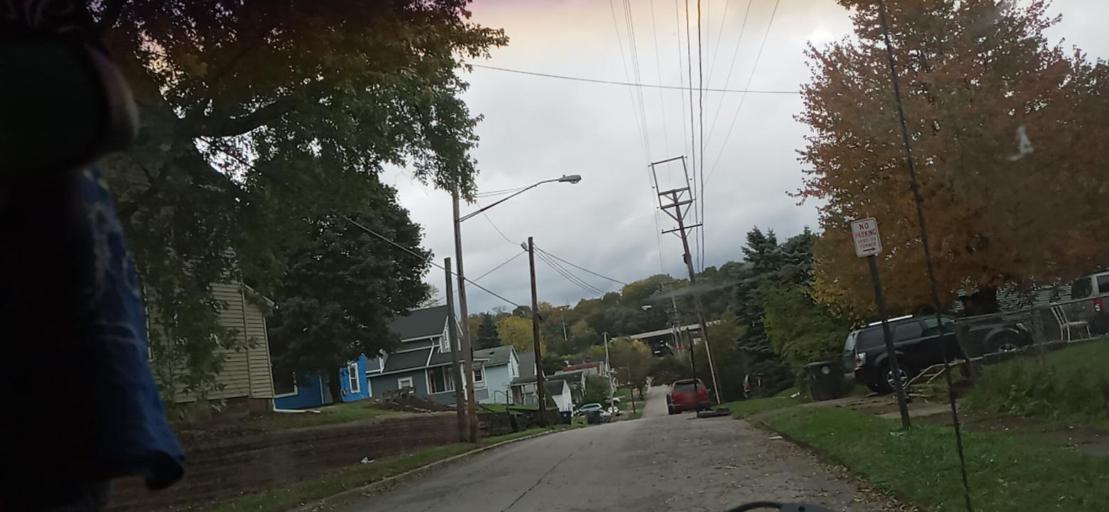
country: US
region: Ohio
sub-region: Summit County
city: Akron
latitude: 41.0679
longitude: -81.5081
